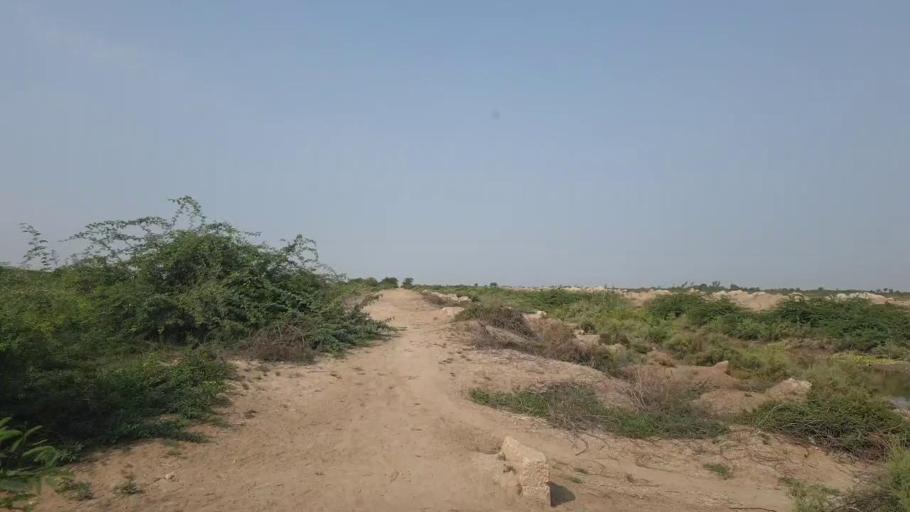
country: PK
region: Sindh
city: Kadhan
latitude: 24.4098
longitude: 68.8241
